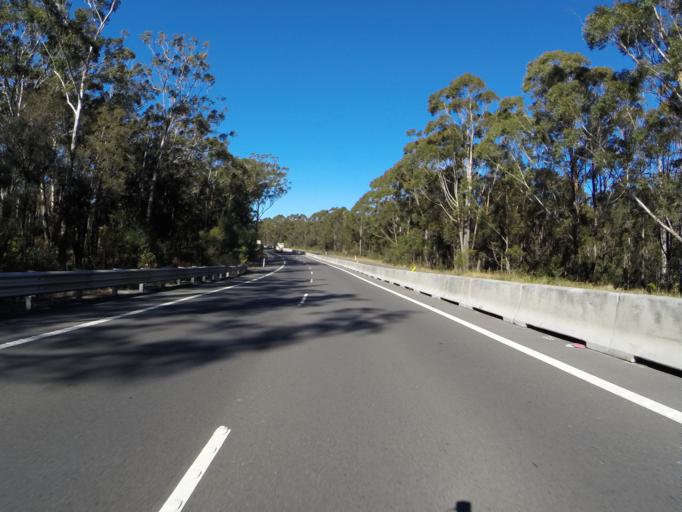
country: AU
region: New South Wales
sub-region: Wollondilly
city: Douglas Park
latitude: -34.2807
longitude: 150.7147
